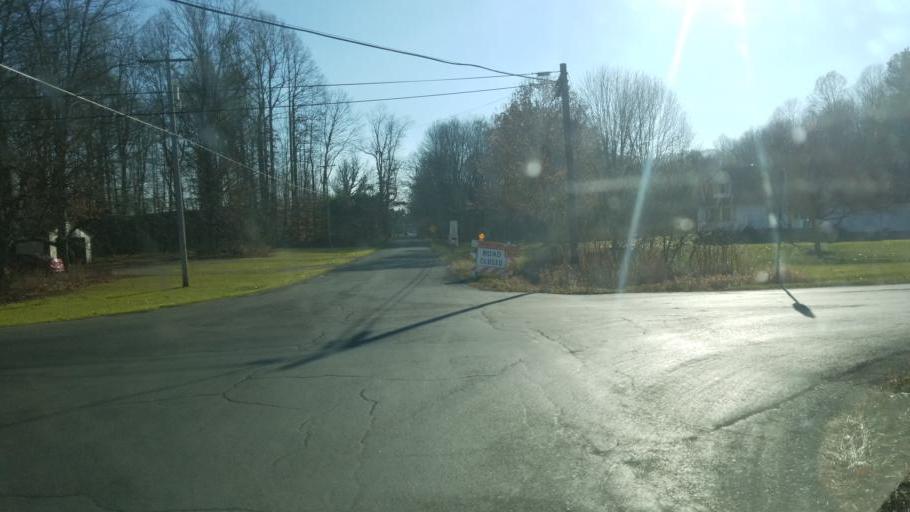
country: US
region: Ohio
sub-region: Portage County
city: Mantua
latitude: 41.3405
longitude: -81.2454
